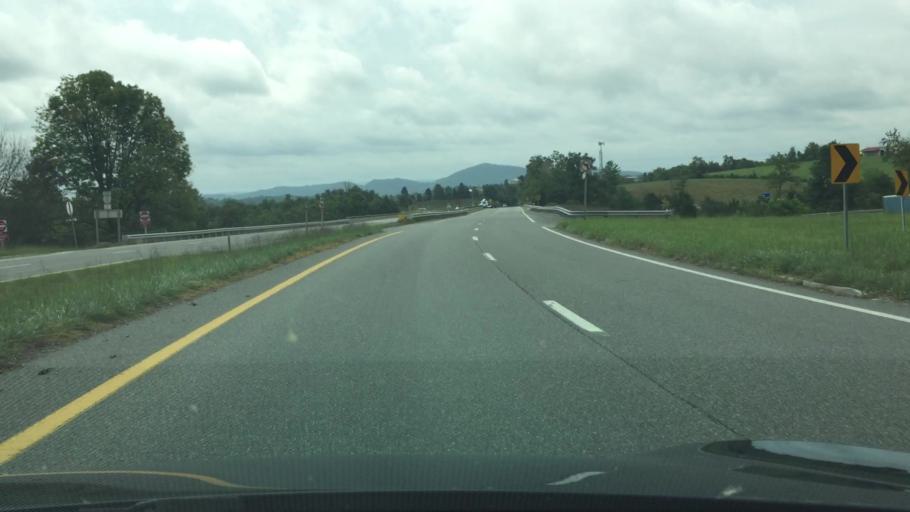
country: US
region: Virginia
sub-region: City of Radford
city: Radford
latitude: 37.0977
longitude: -80.5083
